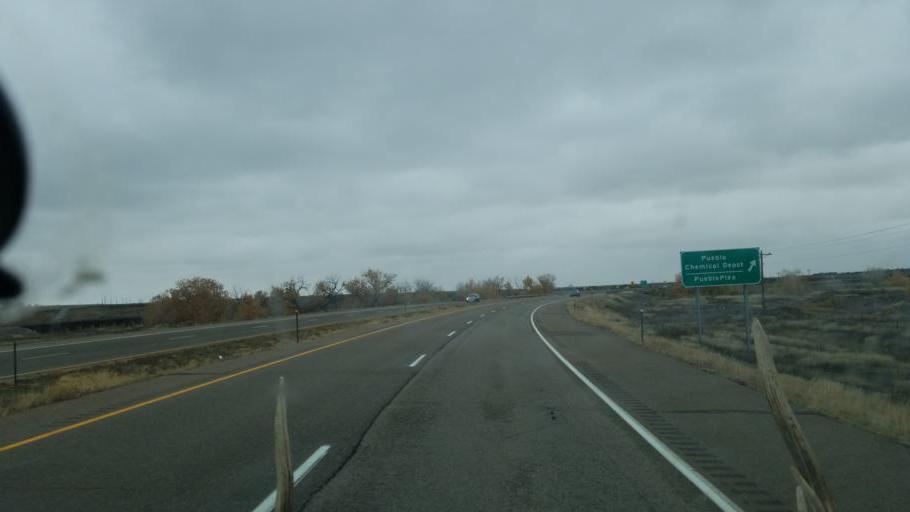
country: US
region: Colorado
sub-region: Pueblo County
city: Pueblo
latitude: 38.2669
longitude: -104.3752
